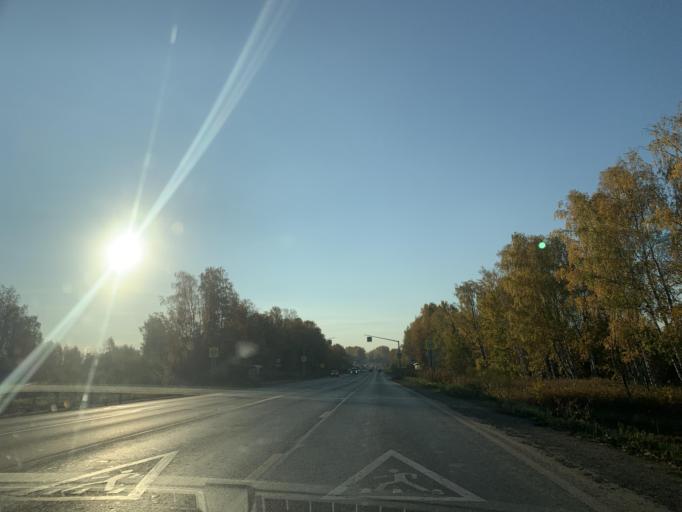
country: RU
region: Jaroslavl
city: Yaroslavl
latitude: 57.7338
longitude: 39.7359
